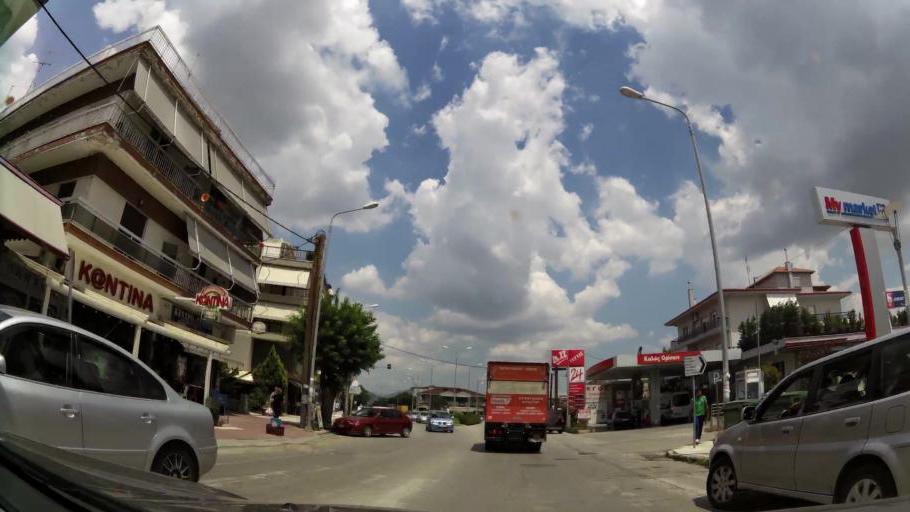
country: GR
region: West Macedonia
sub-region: Nomos Kozanis
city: Kozani
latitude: 40.3001
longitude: 21.7986
